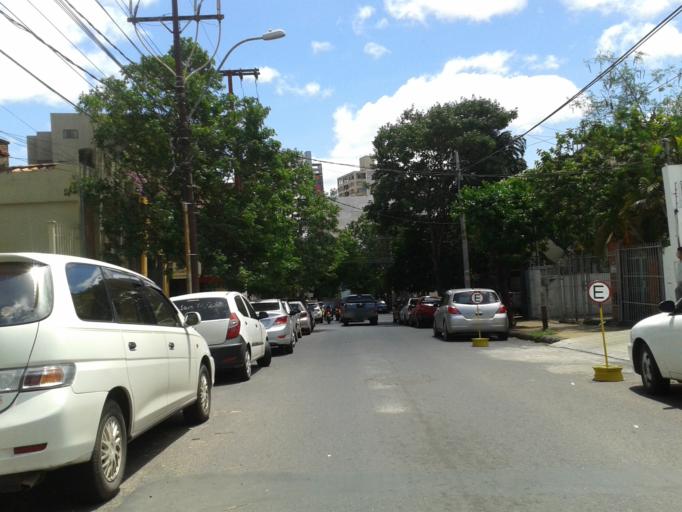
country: PY
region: Asuncion
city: Asuncion
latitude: -25.2898
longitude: -57.6210
